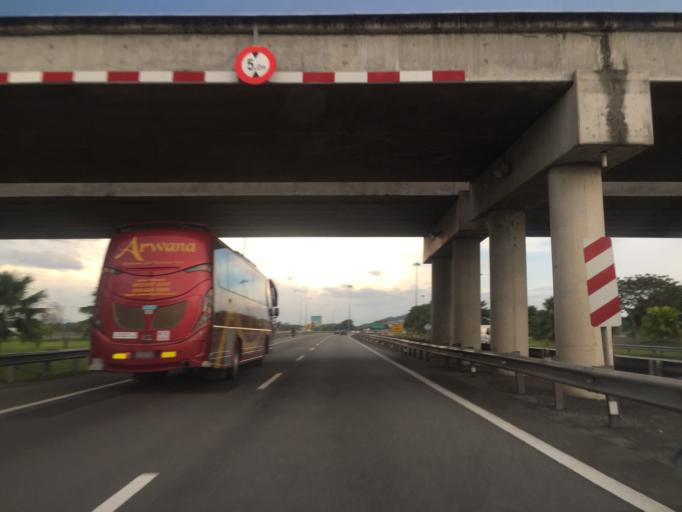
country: MY
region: Kedah
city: Alor Setar
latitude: 5.9792
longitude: 100.4385
